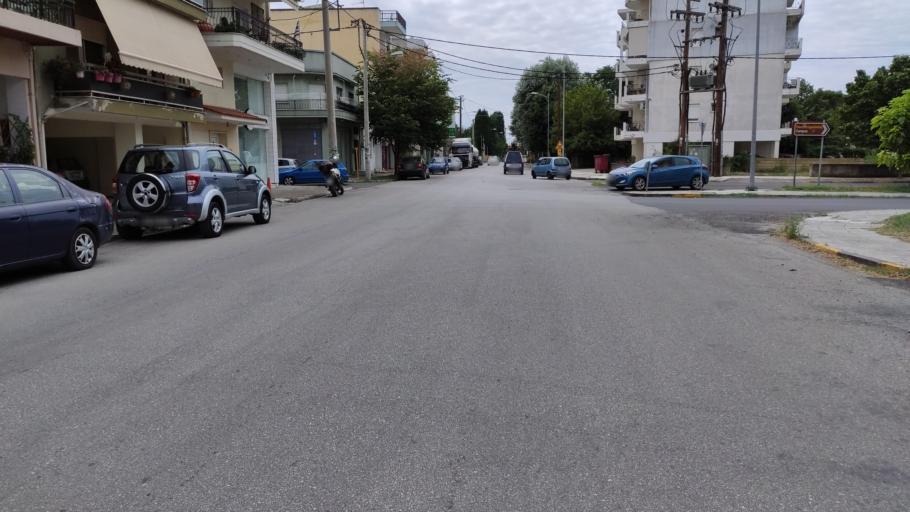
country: GR
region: East Macedonia and Thrace
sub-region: Nomos Rodopis
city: Komotini
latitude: 41.1176
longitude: 25.3908
